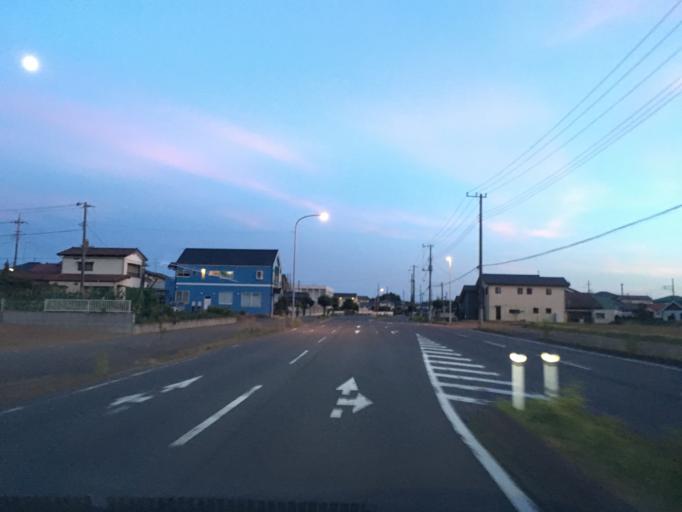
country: JP
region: Ibaraki
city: Hitachi-Naka
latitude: 36.3958
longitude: 140.5546
